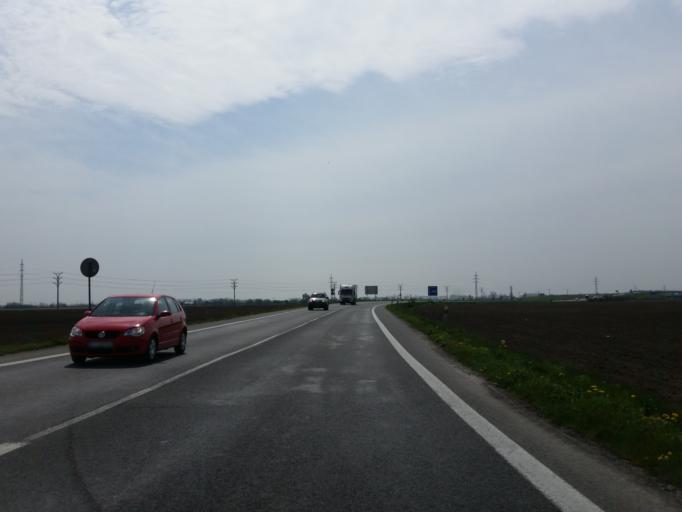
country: SK
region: Trnavsky
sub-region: Okres Galanta
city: Galanta
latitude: 48.1904
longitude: 17.7501
